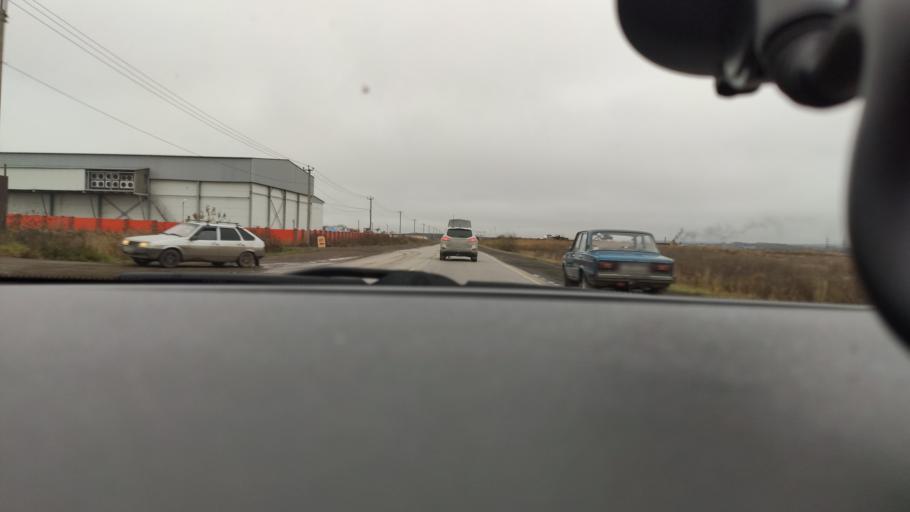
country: RU
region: Perm
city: Froly
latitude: 57.9161
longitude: 56.1860
